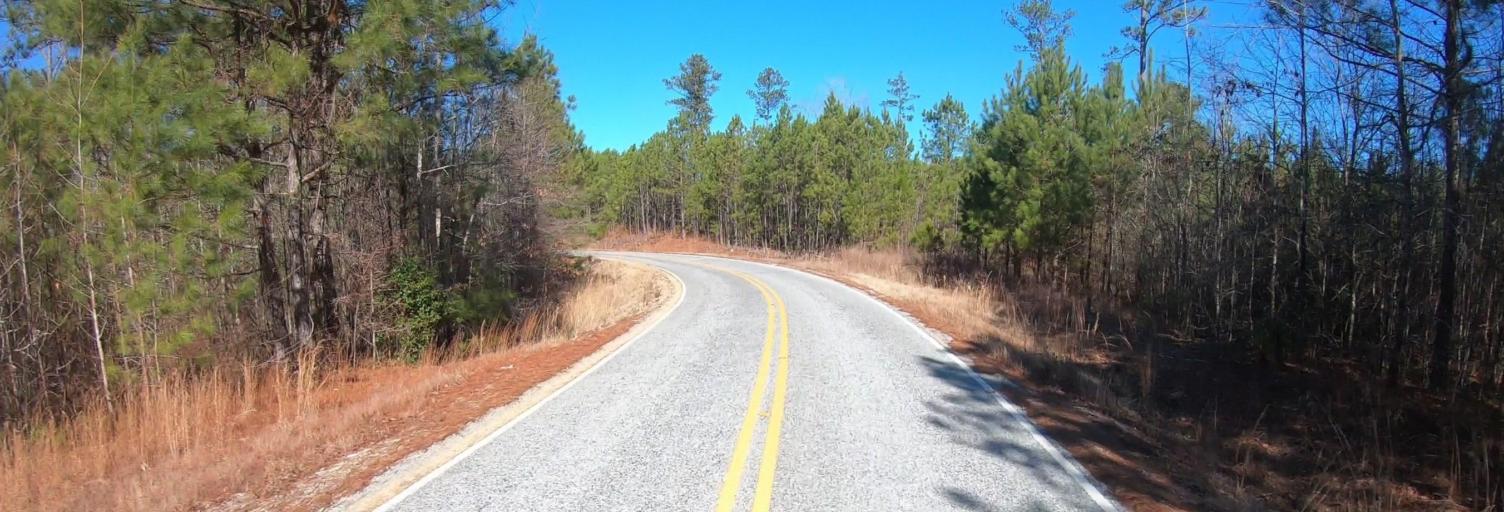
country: US
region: Alabama
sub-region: Clay County
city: Ashland
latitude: 33.3868
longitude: -85.8702
